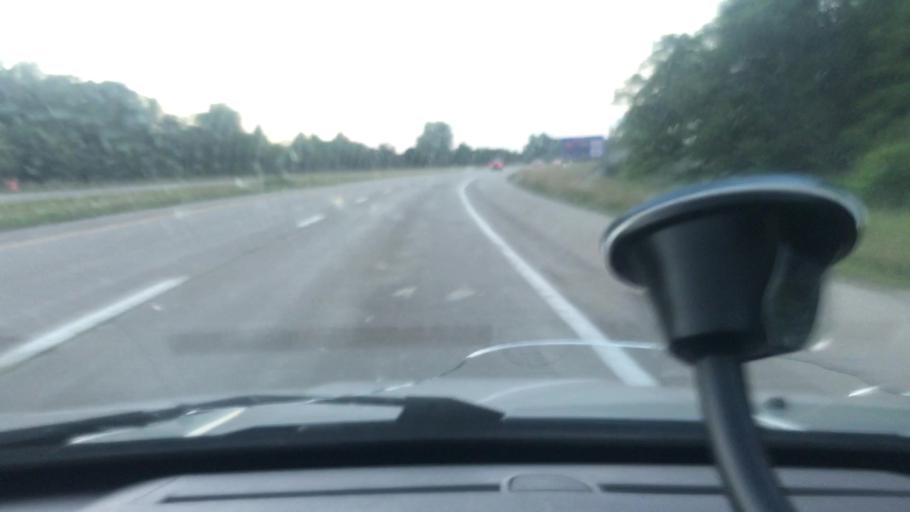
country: US
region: Illinois
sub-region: Peoria County
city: Bellevue
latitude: 40.7501
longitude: -89.6704
